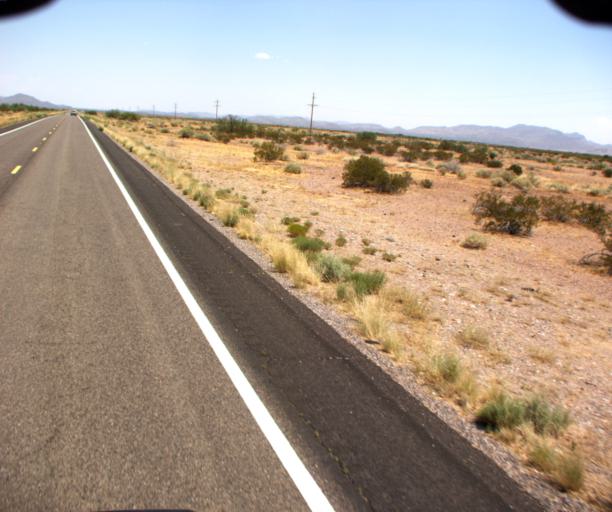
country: US
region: Arizona
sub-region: Graham County
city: Safford
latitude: 32.7782
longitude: -109.5170
